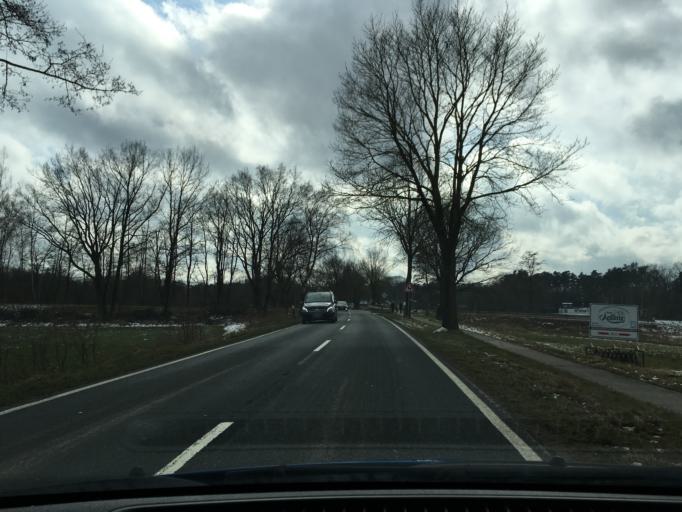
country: DE
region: Lower Saxony
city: Barum
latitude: 53.3400
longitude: 10.4009
